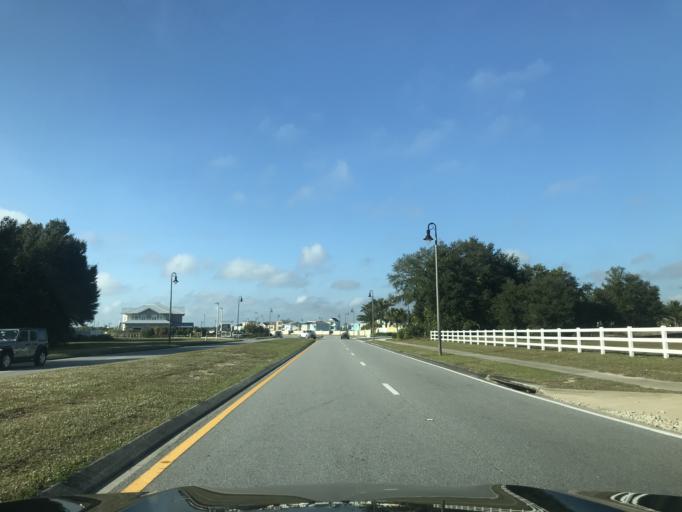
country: US
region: Florida
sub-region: Polk County
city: Citrus Ridge
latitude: 28.3363
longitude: -81.6036
